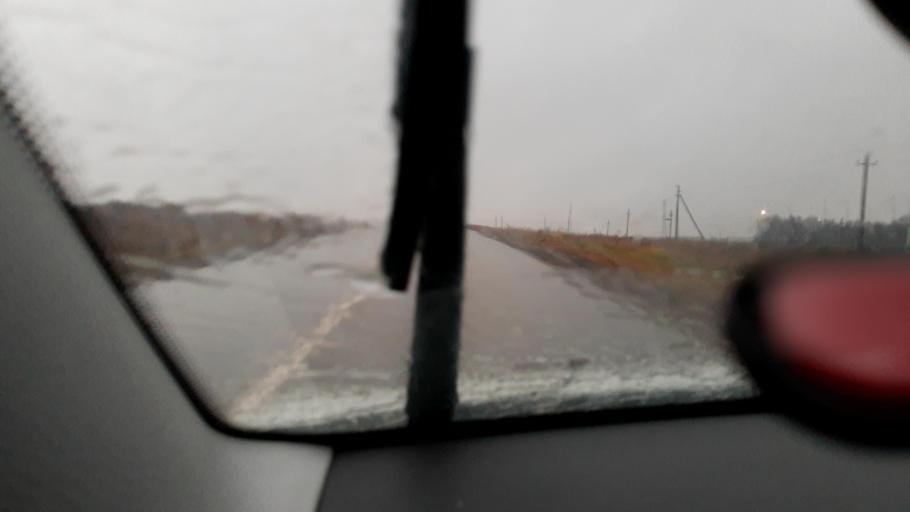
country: RU
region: Bashkortostan
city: Blagoveshchensk
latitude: 54.9008
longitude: 56.1798
